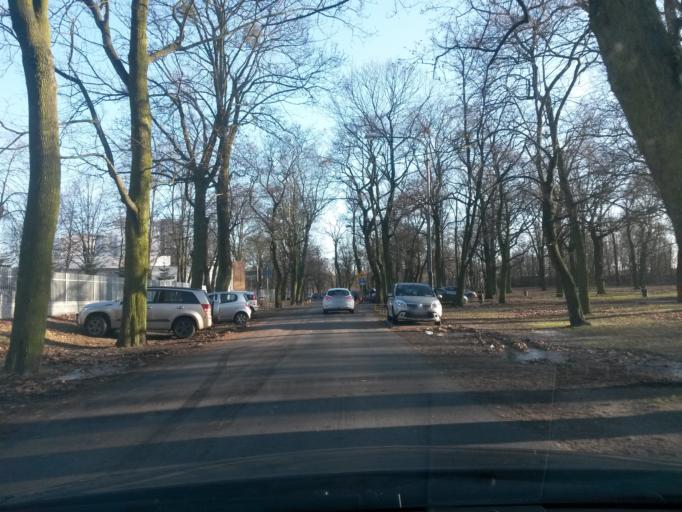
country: PL
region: Greater Poland Voivodeship
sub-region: Poznan
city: Poznan
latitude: 52.4251
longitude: 16.9337
